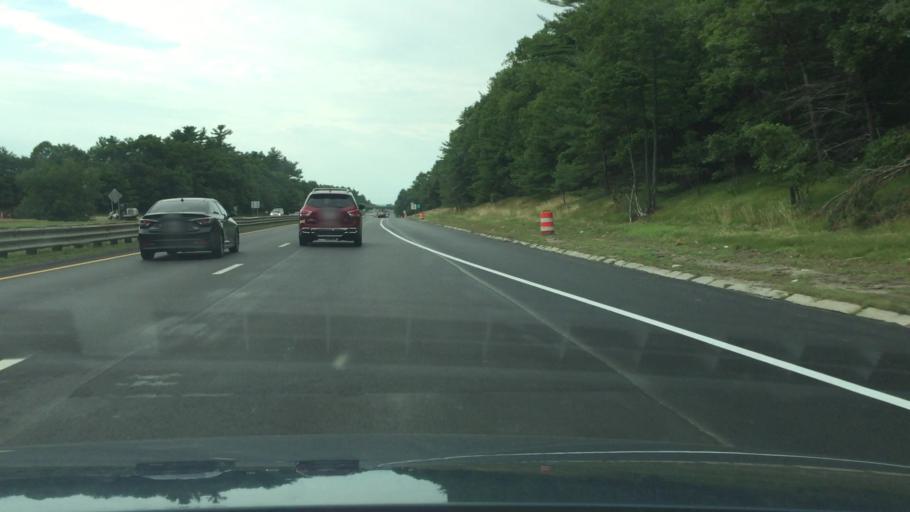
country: US
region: Massachusetts
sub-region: Plymouth County
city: Kingston
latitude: 42.0147
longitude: -70.7264
